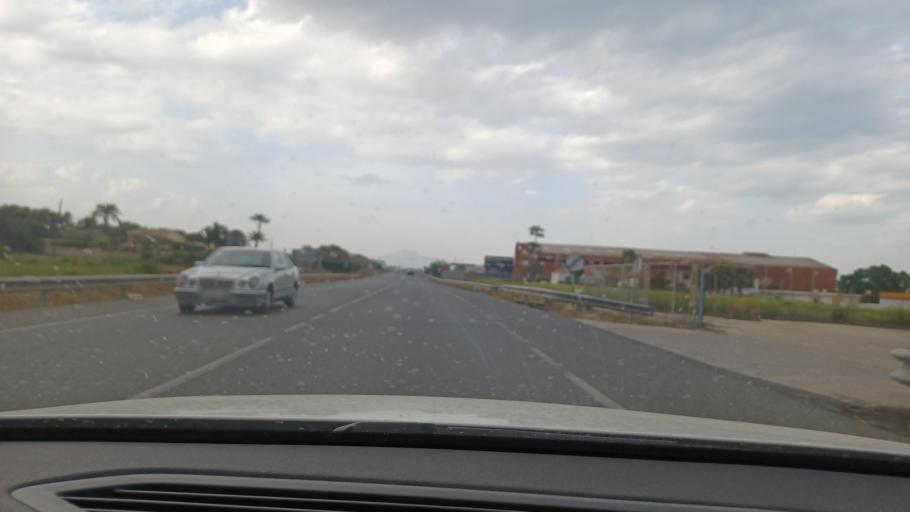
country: ES
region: Valencia
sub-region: Provincia de Castello
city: Benicarlo
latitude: 40.4341
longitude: 0.4386
